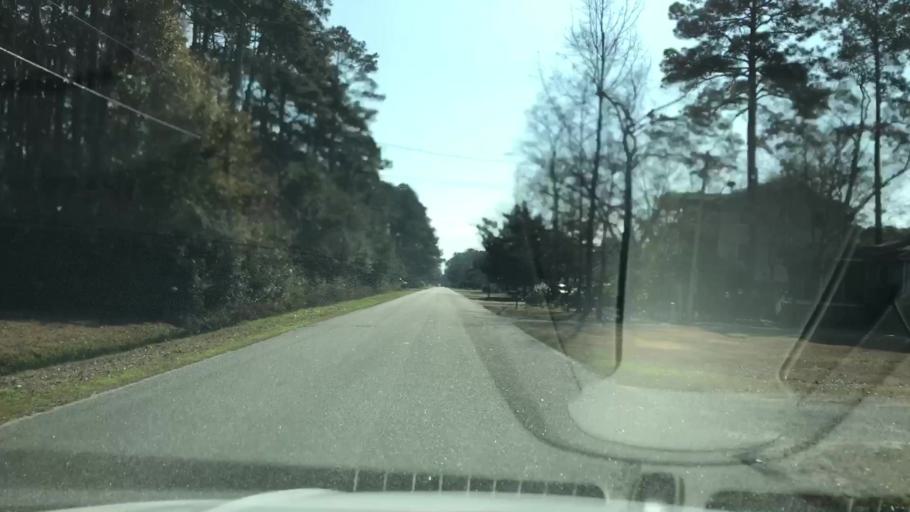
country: US
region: South Carolina
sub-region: Horry County
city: Garden City
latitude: 33.5877
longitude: -79.0062
